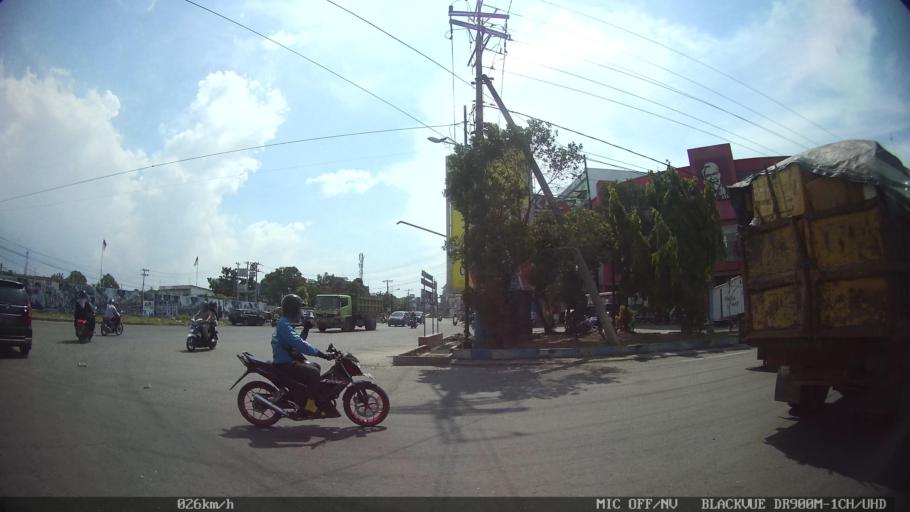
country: ID
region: North Sumatra
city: Medan
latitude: 3.6284
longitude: 98.6617
